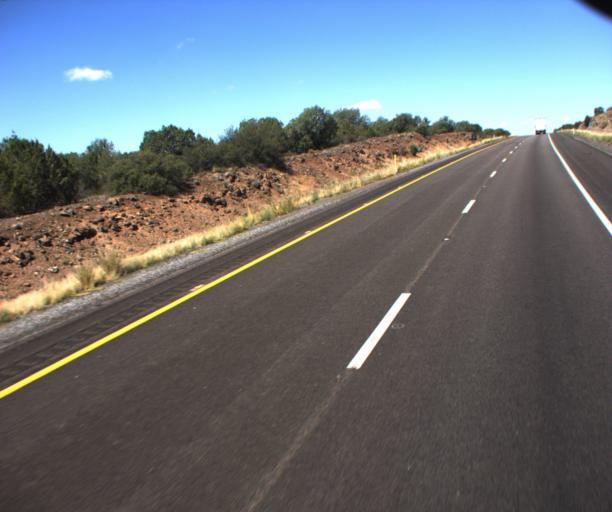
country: US
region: Arizona
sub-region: Mohave County
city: Peach Springs
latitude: 35.1900
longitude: -113.3236
